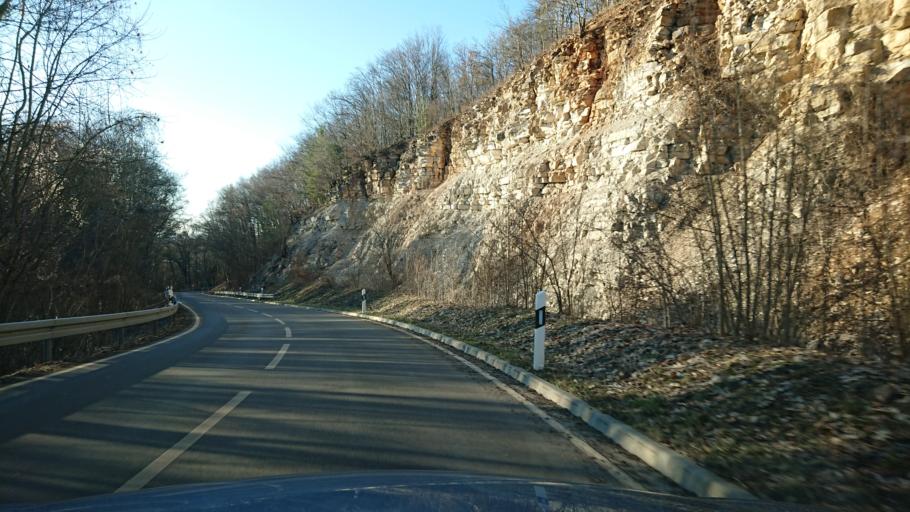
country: DE
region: Bavaria
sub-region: Upper Franconia
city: Weilersbach
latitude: 49.7949
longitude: 11.1255
